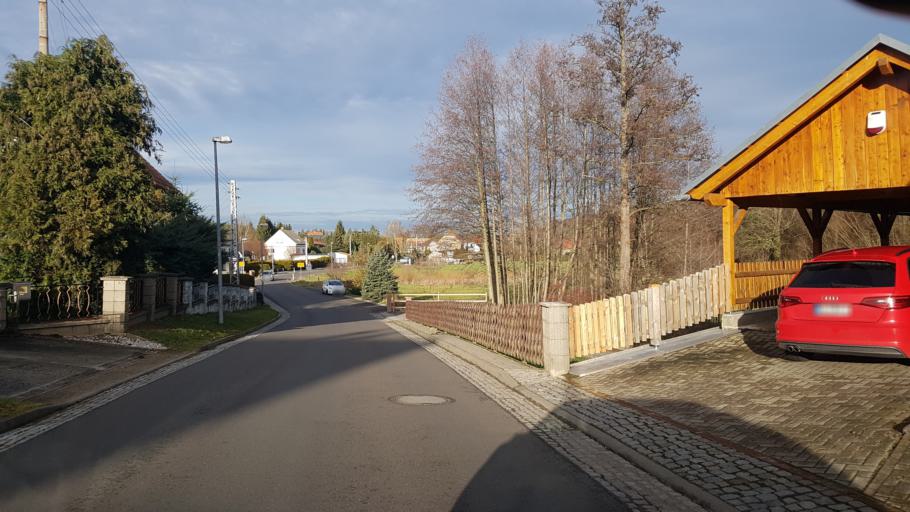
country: DE
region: Saxony
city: Ostrau
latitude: 51.1701
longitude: 13.1624
